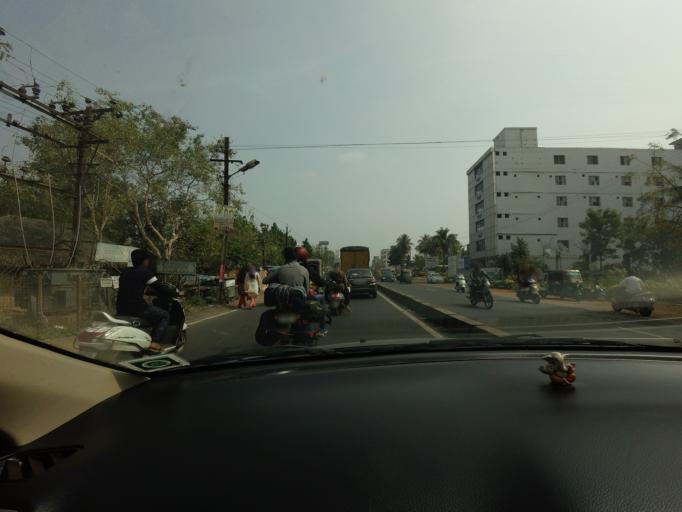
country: IN
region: Andhra Pradesh
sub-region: Krishna
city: Yanamalakuduru
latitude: 16.4884
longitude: 80.6757
